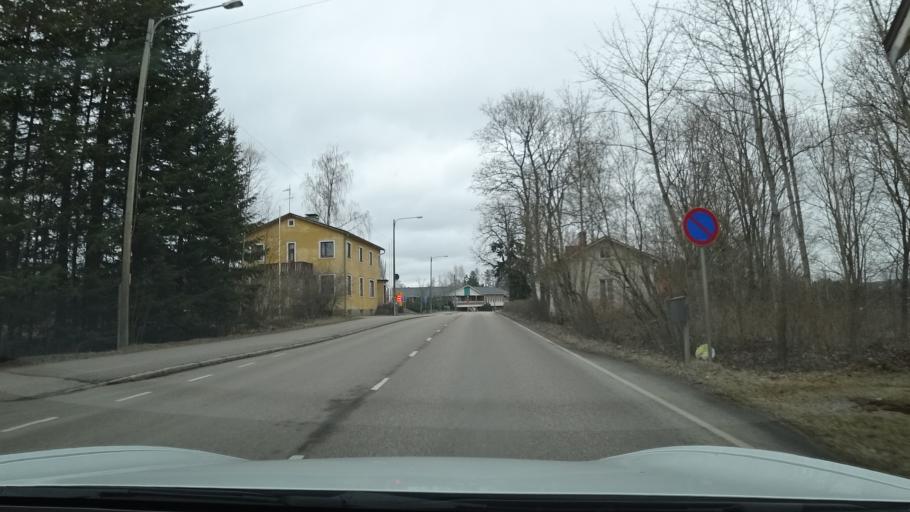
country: FI
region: Uusimaa
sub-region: Porvoo
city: Myrskylae
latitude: 60.6684
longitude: 25.8525
